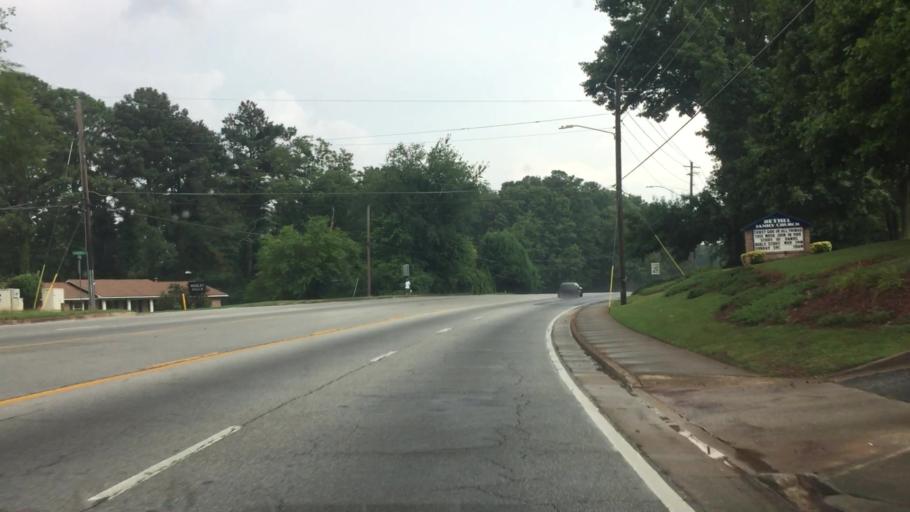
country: US
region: Georgia
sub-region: DeKalb County
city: Candler-McAfee
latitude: 33.7239
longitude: -84.2143
